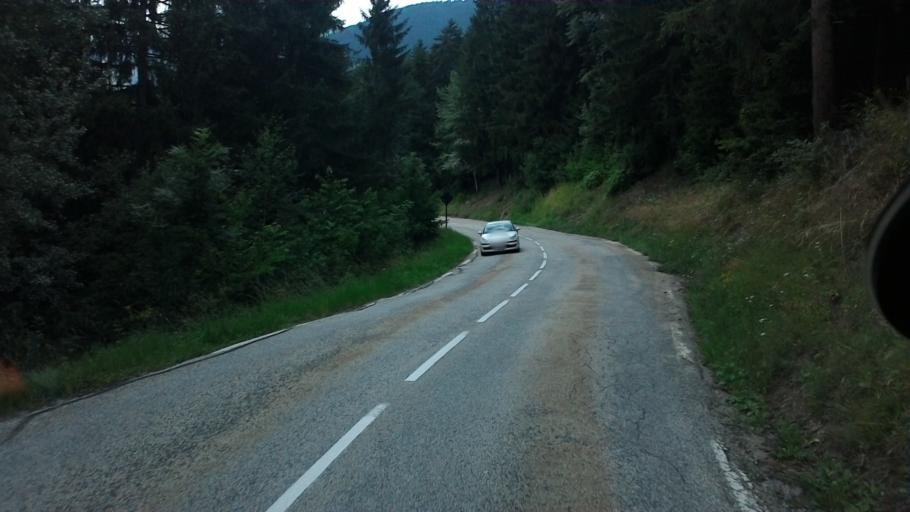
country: FR
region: Rhone-Alpes
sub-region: Departement de la Savoie
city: Seez
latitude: 45.6213
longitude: 6.8231
